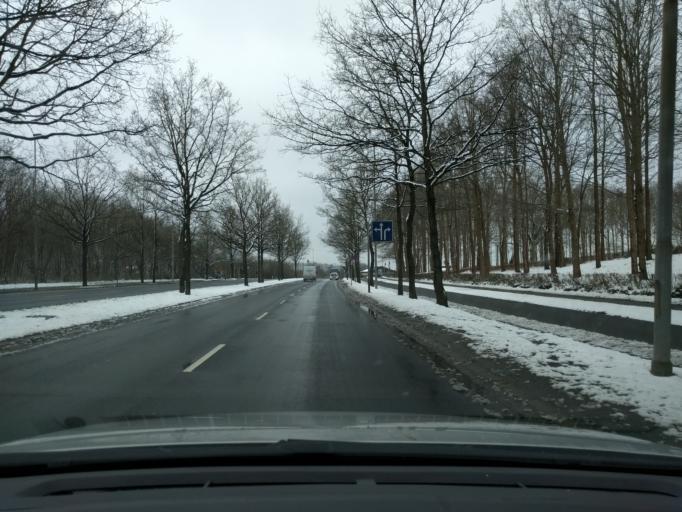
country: DK
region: South Denmark
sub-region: Odense Kommune
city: Seden
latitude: 55.4034
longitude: 10.4427
